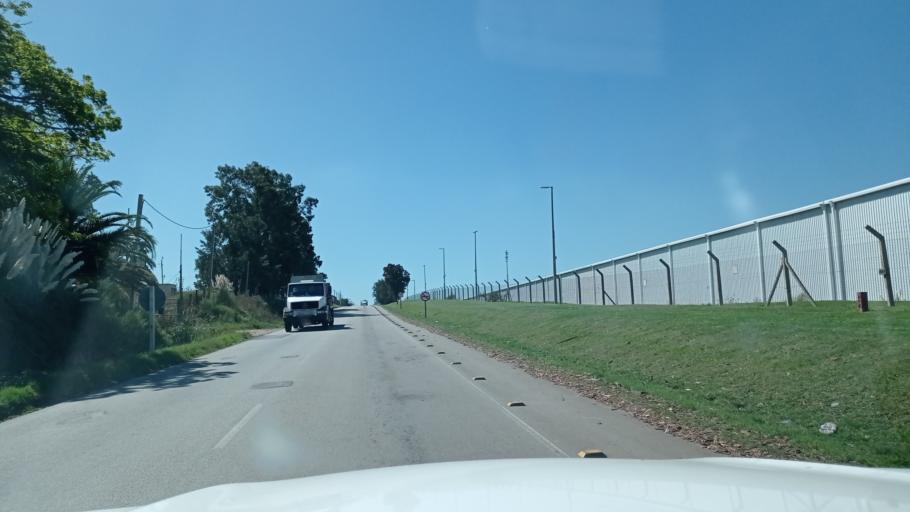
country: UY
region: Montevideo
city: Pajas Blancas
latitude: -34.8571
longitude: -56.2893
